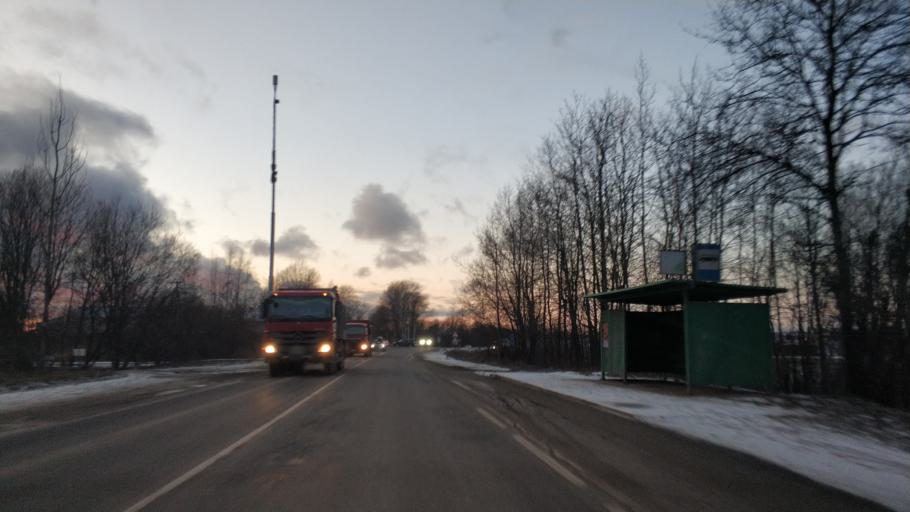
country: RU
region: St.-Petersburg
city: Pontonnyy
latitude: 59.8070
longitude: 30.6201
